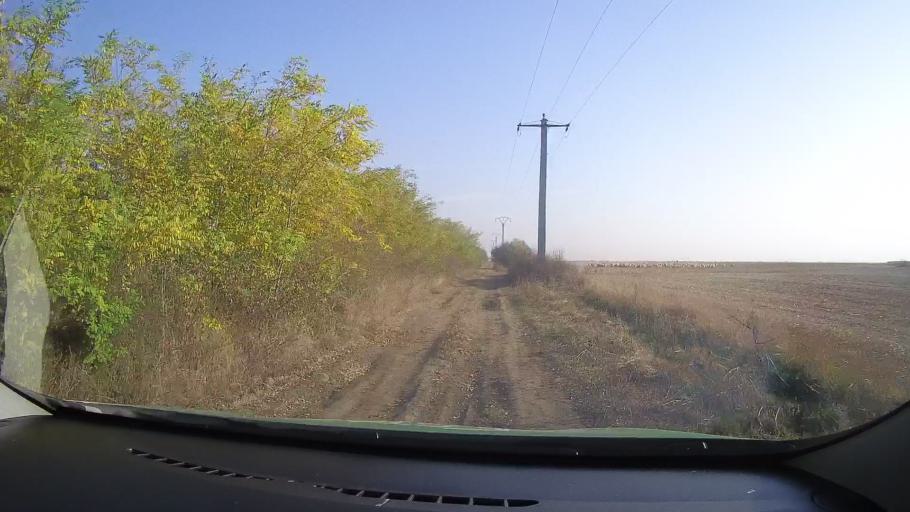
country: RO
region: Arad
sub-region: Comuna Graniceri
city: Graniceri
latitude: 46.5362
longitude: 21.3223
